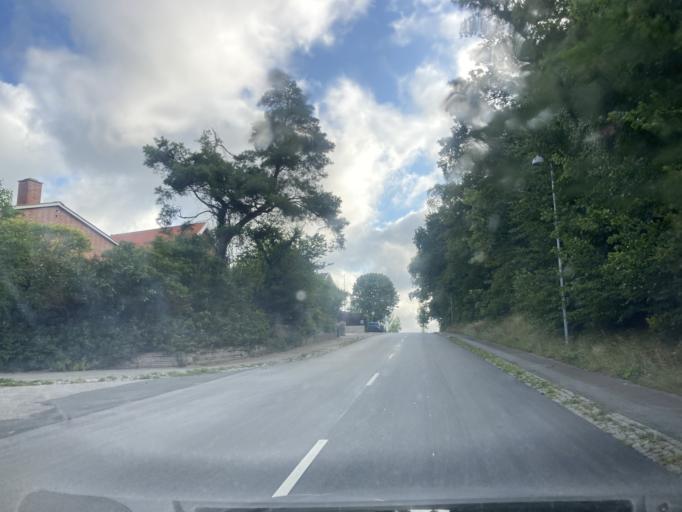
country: DK
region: Capital Region
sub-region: Halsnaes Kommune
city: Frederiksvaerk
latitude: 55.9771
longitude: 12.0222
